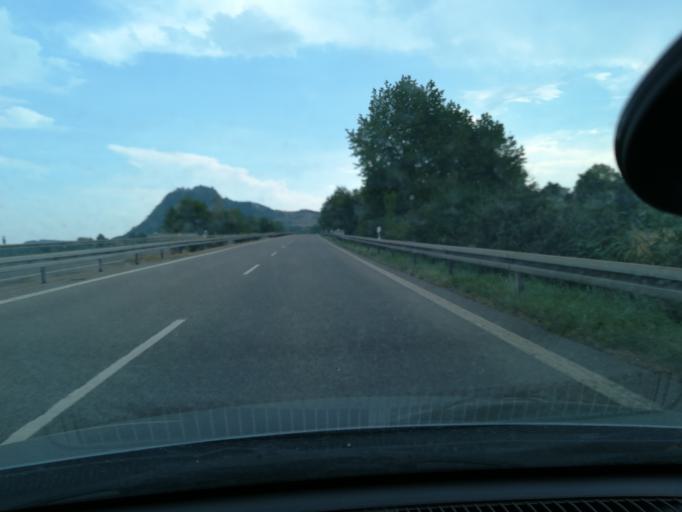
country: DE
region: Baden-Wuerttemberg
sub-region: Freiburg Region
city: Singen
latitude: 47.7853
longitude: 8.8281
